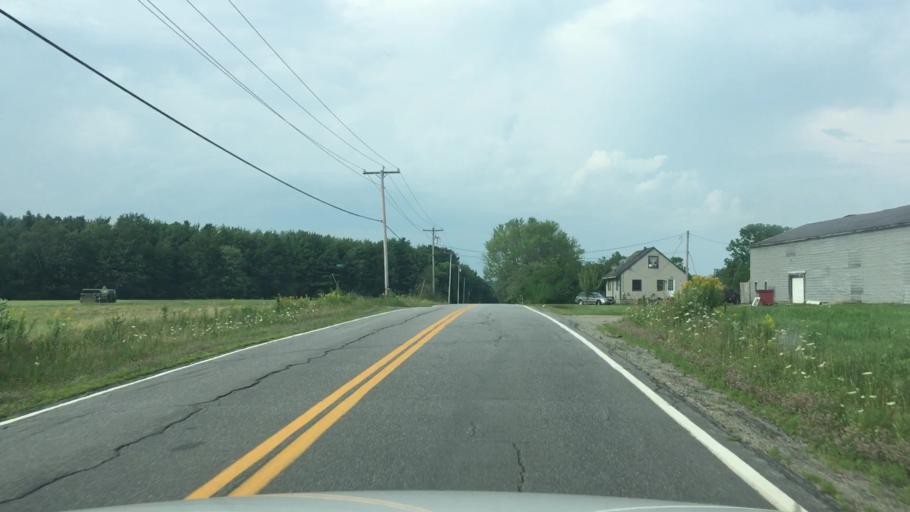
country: US
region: Maine
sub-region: Knox County
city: Washington
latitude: 44.2828
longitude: -69.3673
